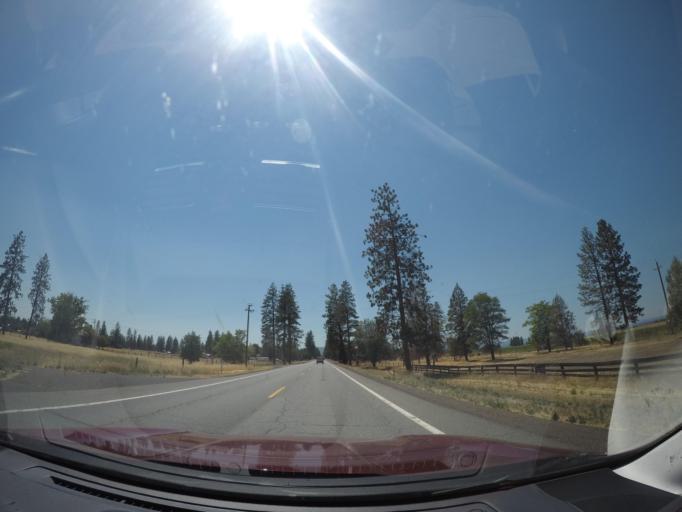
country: US
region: California
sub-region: Shasta County
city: Burney
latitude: 41.0671
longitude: -121.3501
